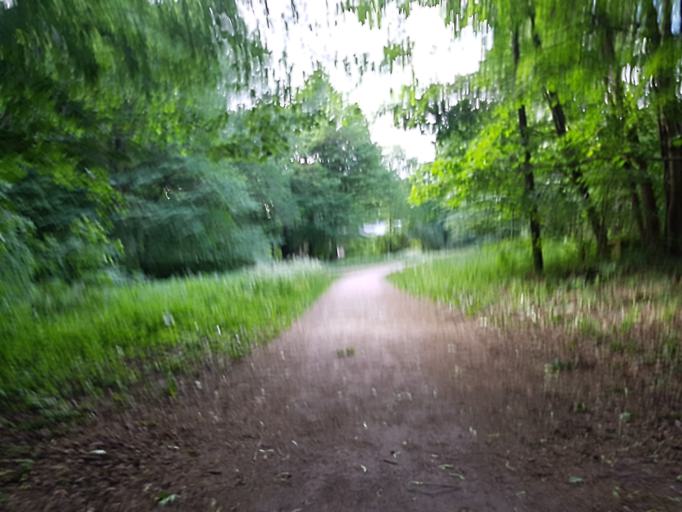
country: FI
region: Uusimaa
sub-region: Helsinki
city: Teekkarikylae
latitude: 60.2488
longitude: 24.8708
